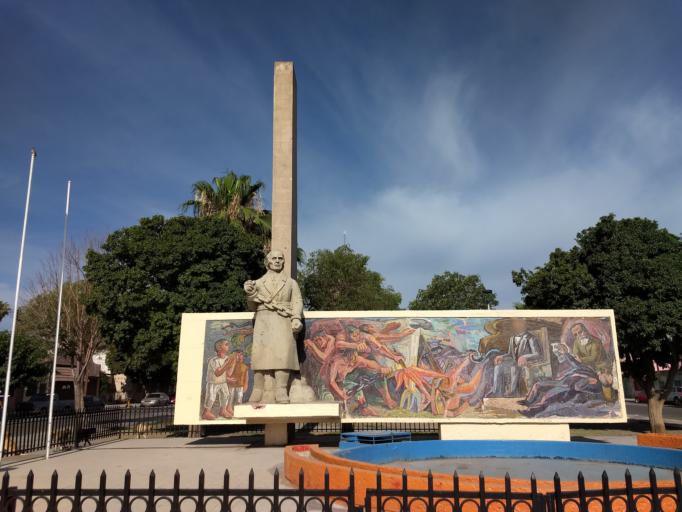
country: MX
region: Durango
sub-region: Lerdo
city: El Huarache (El Guarache)
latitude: 25.5414
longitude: -103.4682
